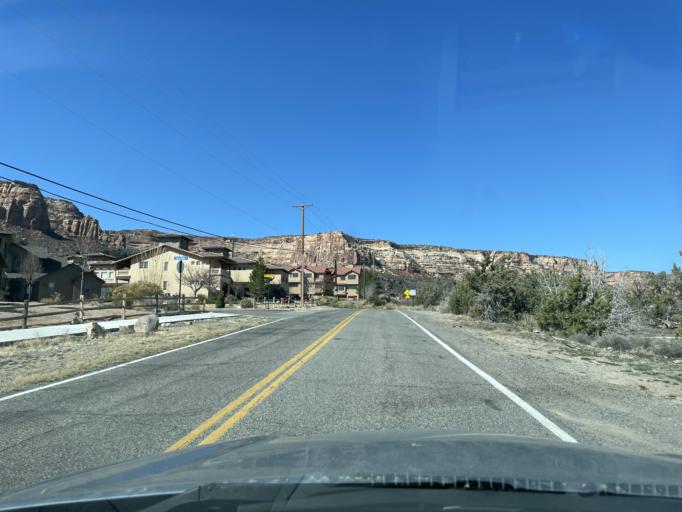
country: US
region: Colorado
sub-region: Mesa County
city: Redlands
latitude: 39.0779
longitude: -108.6670
